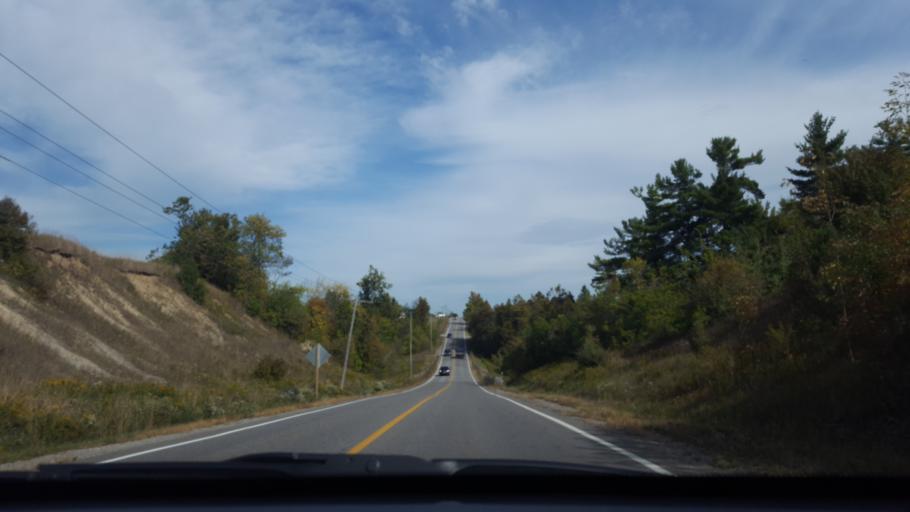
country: CA
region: Ontario
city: Vaughan
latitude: 43.8586
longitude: -79.5884
